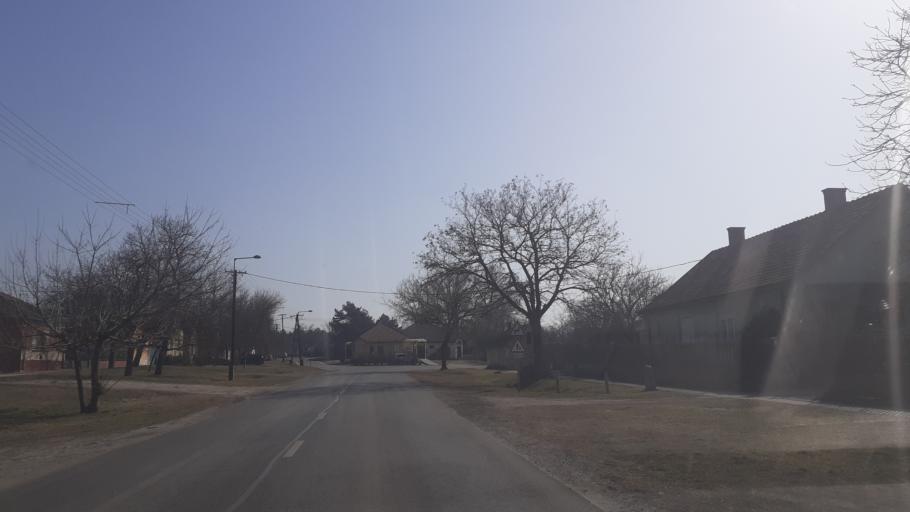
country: HU
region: Pest
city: Orkeny
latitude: 47.0788
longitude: 19.3734
